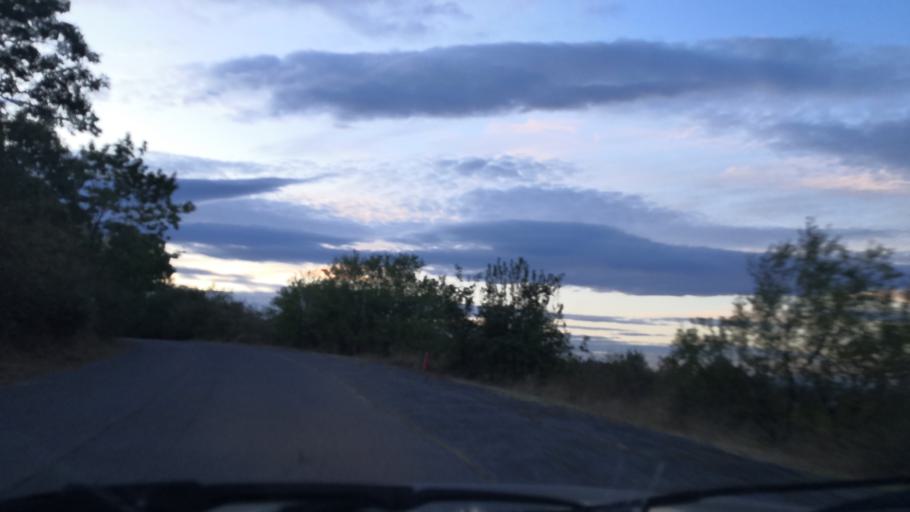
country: RO
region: Mehedinti
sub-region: Comuna Gogosu
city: Balta Verde
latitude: 44.3034
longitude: 22.5520
